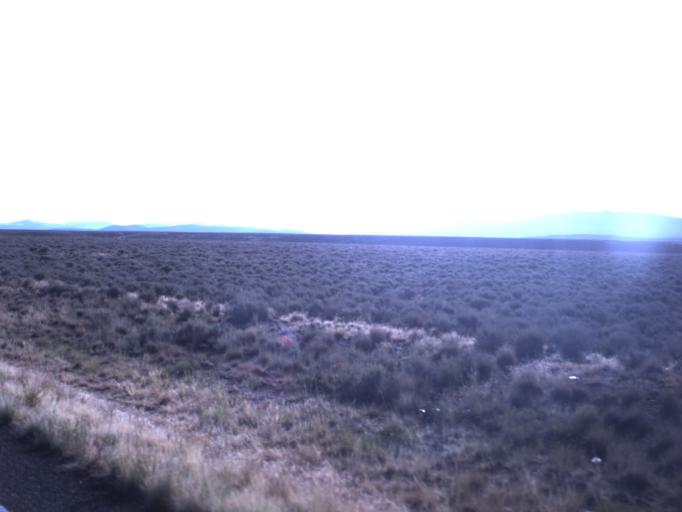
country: US
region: Utah
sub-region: Iron County
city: Enoch
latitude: 37.9586
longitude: -113.0099
